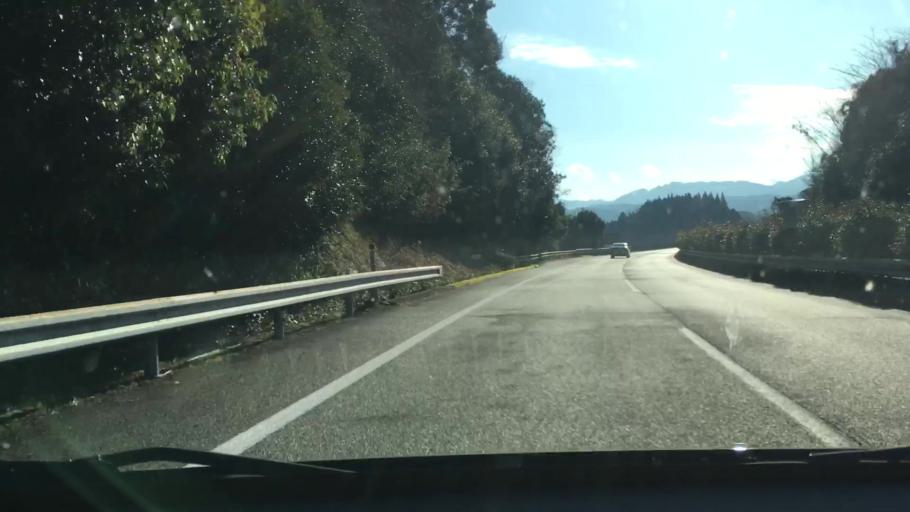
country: JP
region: Kumamoto
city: Hitoyoshi
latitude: 32.2164
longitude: 130.7795
